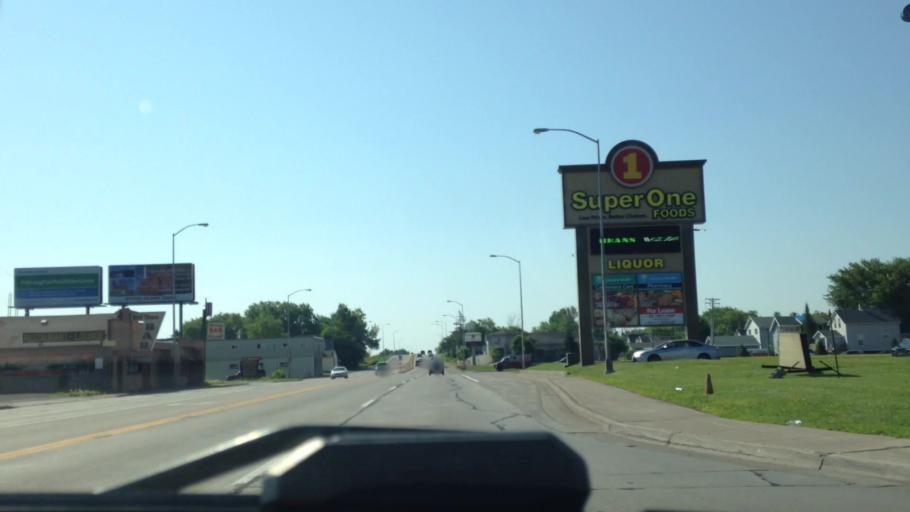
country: US
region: Wisconsin
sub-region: Douglas County
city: Superior
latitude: 46.7065
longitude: -92.0474
